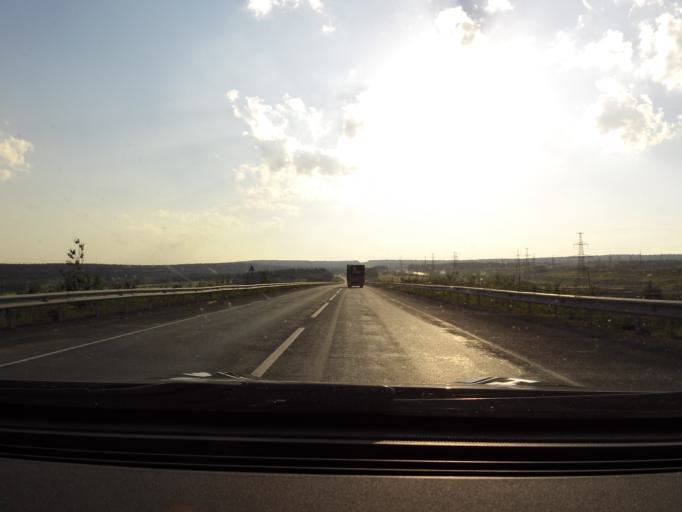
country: RU
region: Sverdlovsk
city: Revda
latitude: 56.8268
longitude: 59.9041
